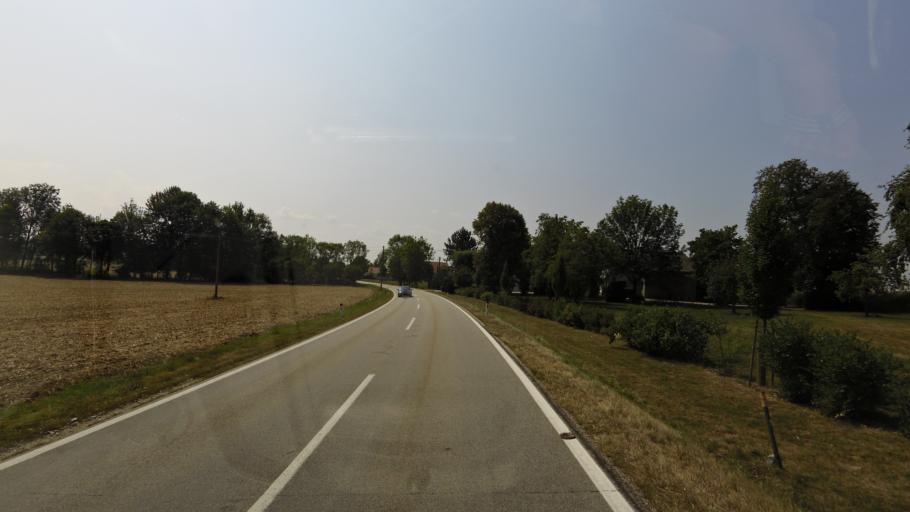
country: DE
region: Bavaria
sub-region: Lower Bavaria
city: Bad Fussing
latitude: 48.2923
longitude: 13.3284
